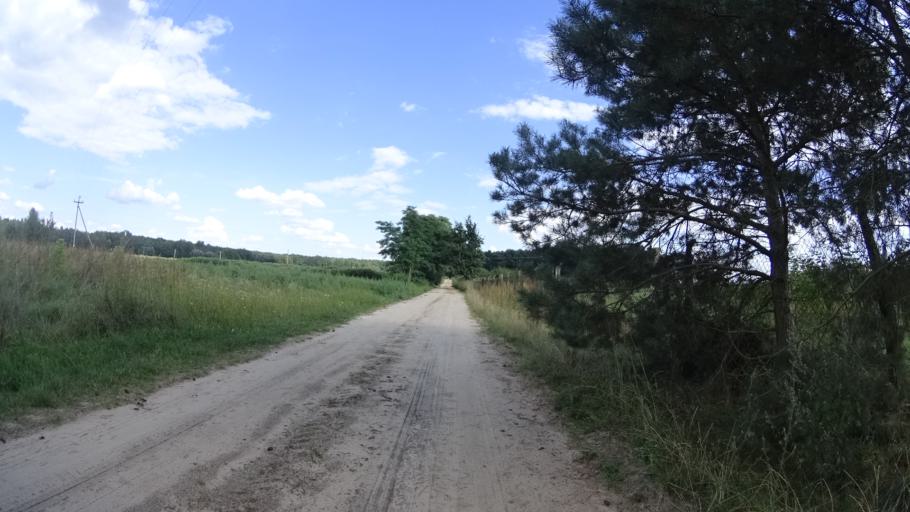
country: PL
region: Masovian Voivodeship
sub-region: Powiat grojecki
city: Mogielnica
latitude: 51.6779
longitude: 20.7676
